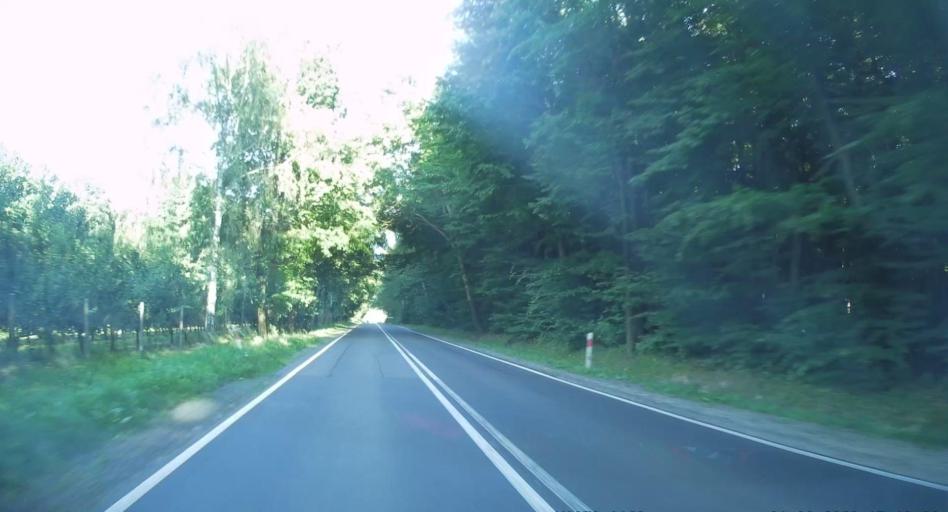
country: PL
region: Lodz Voivodeship
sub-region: Powiat rawski
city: Sadkowice
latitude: 51.8049
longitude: 20.5858
